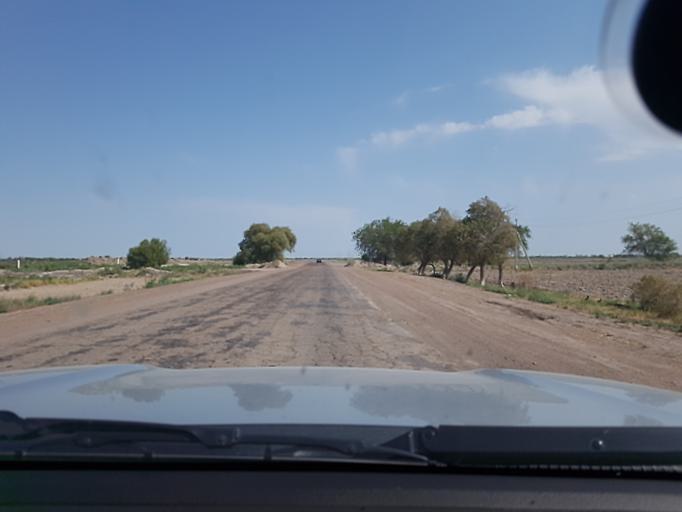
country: TM
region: Dasoguz
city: Boldumsaz
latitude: 42.1928
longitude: 59.5486
